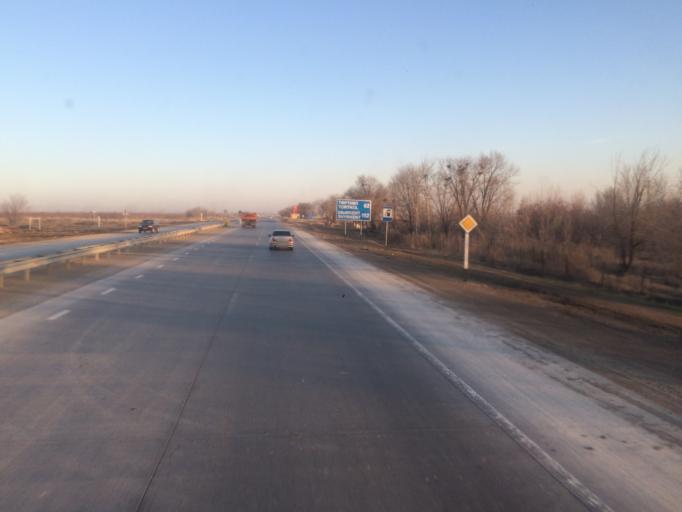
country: KZ
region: Ongtustik Qazaqstan
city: Turkestan
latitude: 43.2712
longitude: 68.3470
